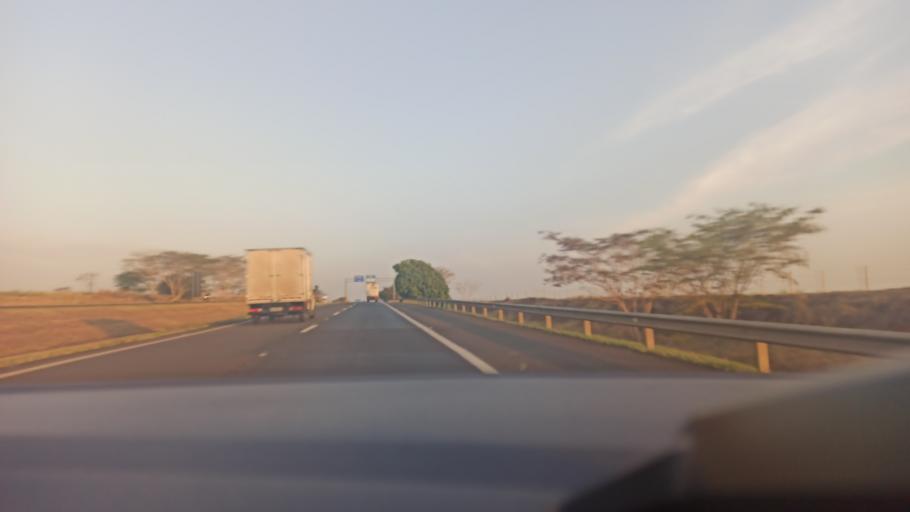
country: BR
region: Sao Paulo
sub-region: Santa Adelia
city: Santa Adelia
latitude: -21.3768
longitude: -48.7413
